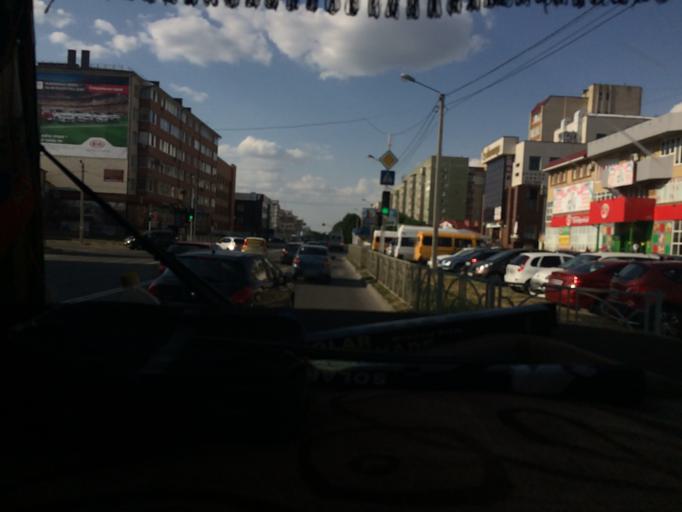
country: RU
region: Stavropol'skiy
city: Tatarka
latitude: 45.0075
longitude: 41.9127
